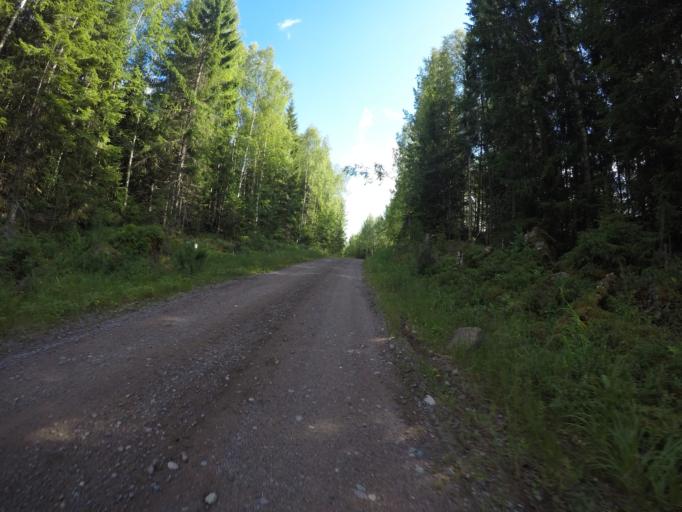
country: SE
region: OErebro
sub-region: Hallefors Kommun
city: Haellefors
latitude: 59.9951
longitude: 14.6057
